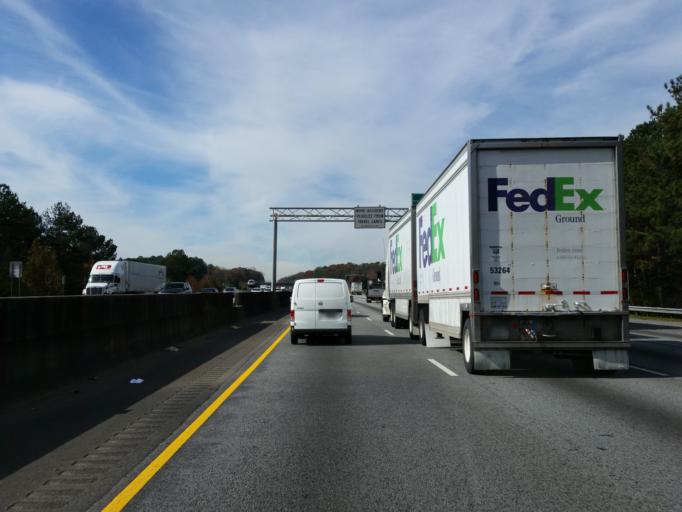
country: US
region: Georgia
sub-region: Cobb County
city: Mableton
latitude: 33.7731
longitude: -84.5533
